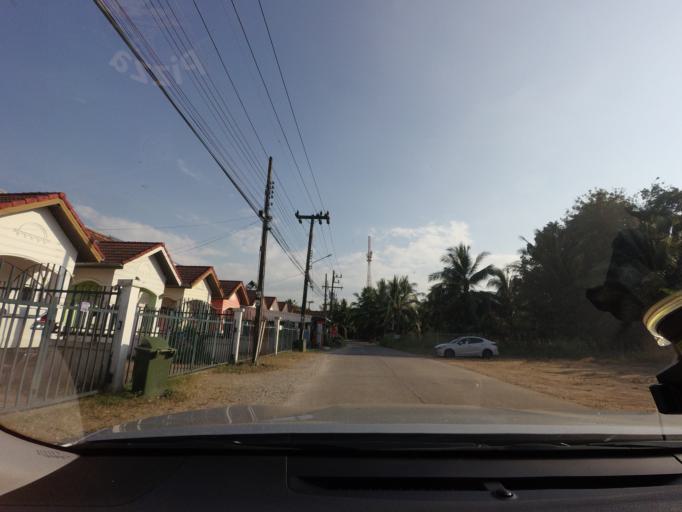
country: TH
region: Phangnga
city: Ban Khao Lak
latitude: 8.6899
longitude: 98.2518
